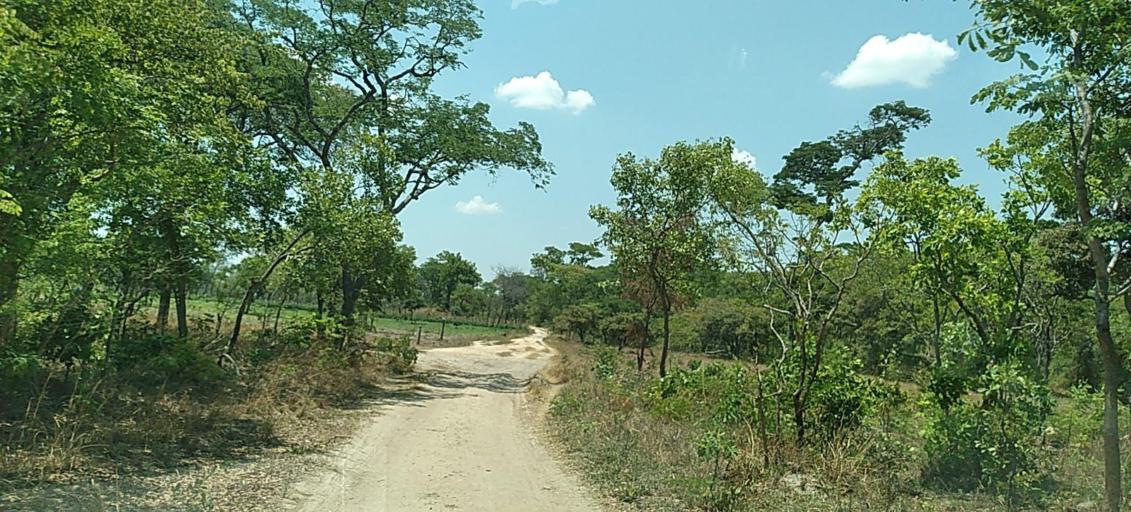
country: ZM
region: Copperbelt
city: Mpongwe
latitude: -13.6507
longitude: 28.4872
